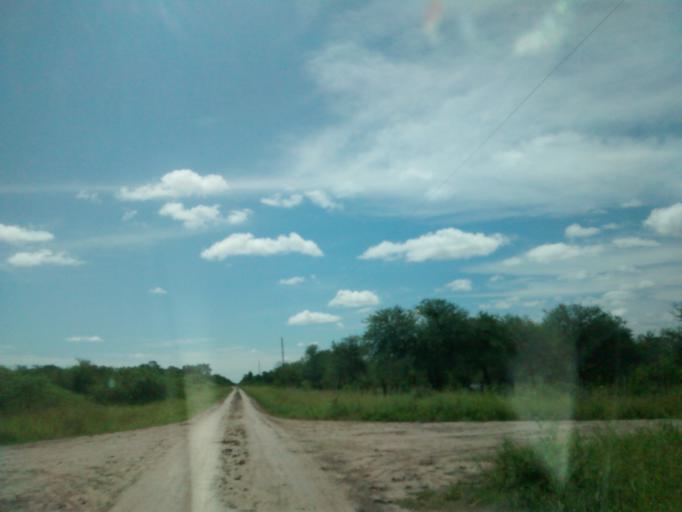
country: AR
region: Chaco
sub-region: Departamento de Quitilipi
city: Quitilipi
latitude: -26.7803
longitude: -60.2322
